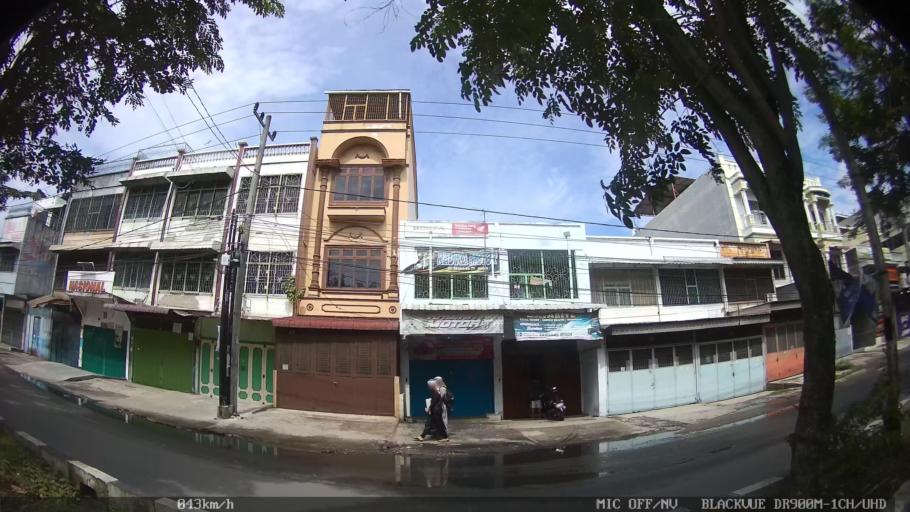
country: ID
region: North Sumatra
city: Medan
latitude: 3.5896
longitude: 98.7060
